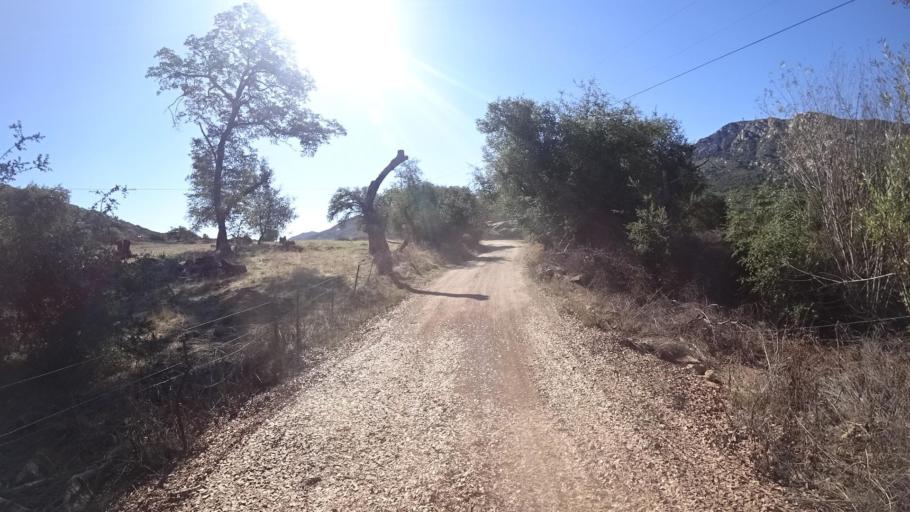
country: US
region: California
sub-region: San Diego County
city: Alpine
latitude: 32.7186
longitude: -116.7577
